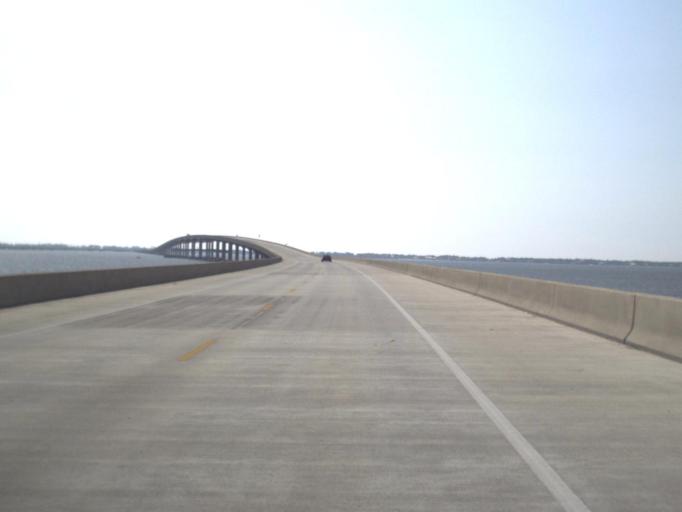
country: US
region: Florida
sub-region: Franklin County
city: Eastpoint
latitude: 29.6914
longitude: -84.8870
